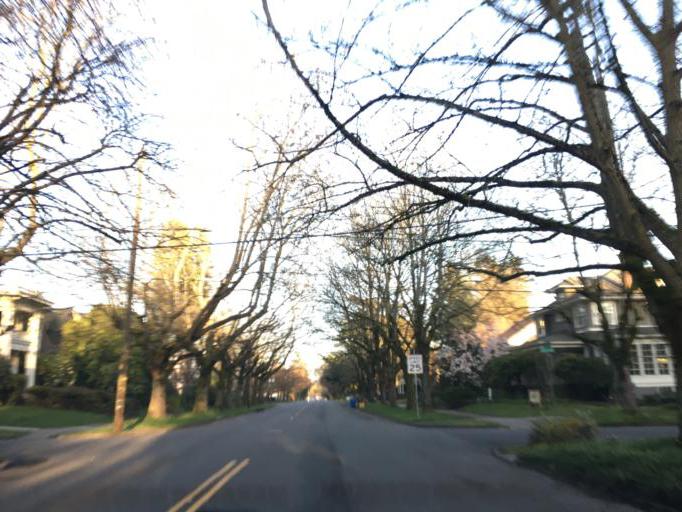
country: US
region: Oregon
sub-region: Multnomah County
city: Portland
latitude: 45.5421
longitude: -122.6499
